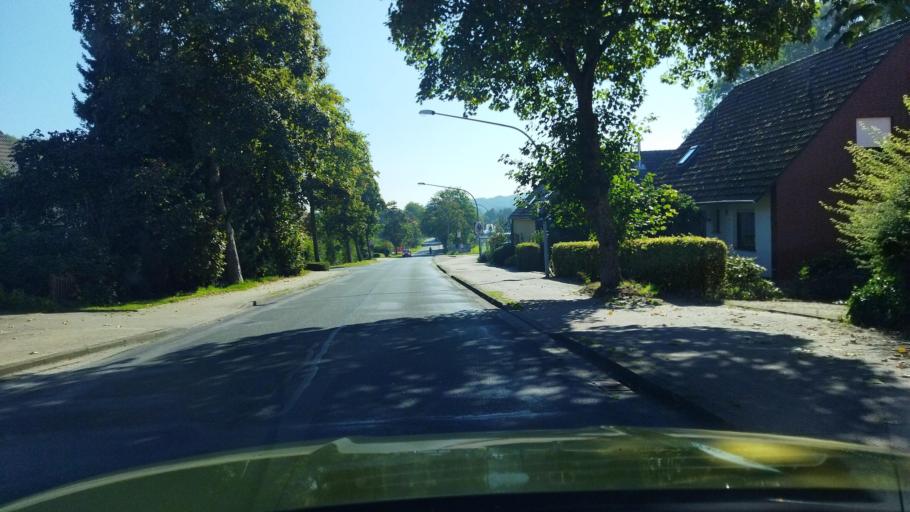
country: DE
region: Lower Saxony
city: Ostercappeln
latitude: 52.3431
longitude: 8.2382
